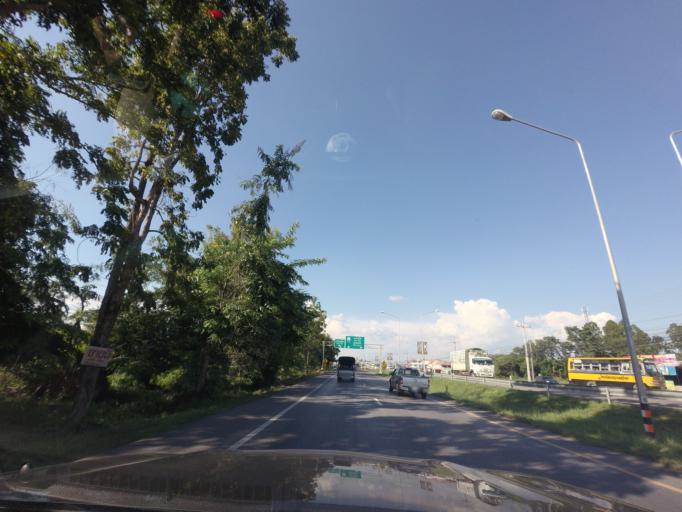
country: TH
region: Khon Kaen
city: Non Sila
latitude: 15.9638
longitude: 102.6906
